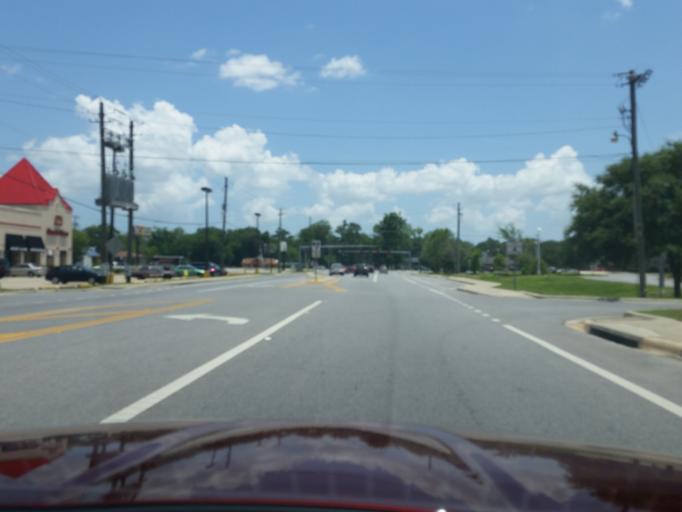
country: US
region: Florida
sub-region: Escambia County
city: Ensley
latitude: 30.5349
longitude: -87.2624
